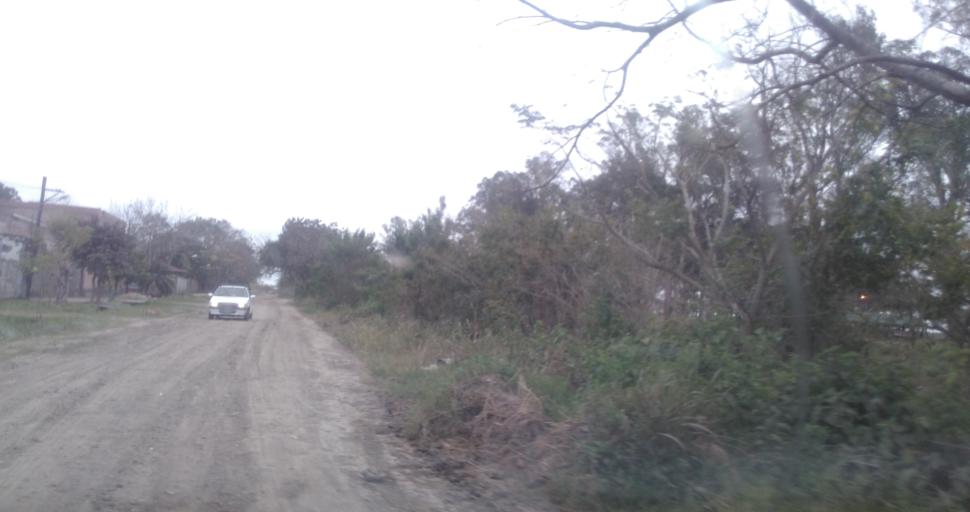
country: AR
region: Chaco
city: Fontana
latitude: -27.4426
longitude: -59.0336
